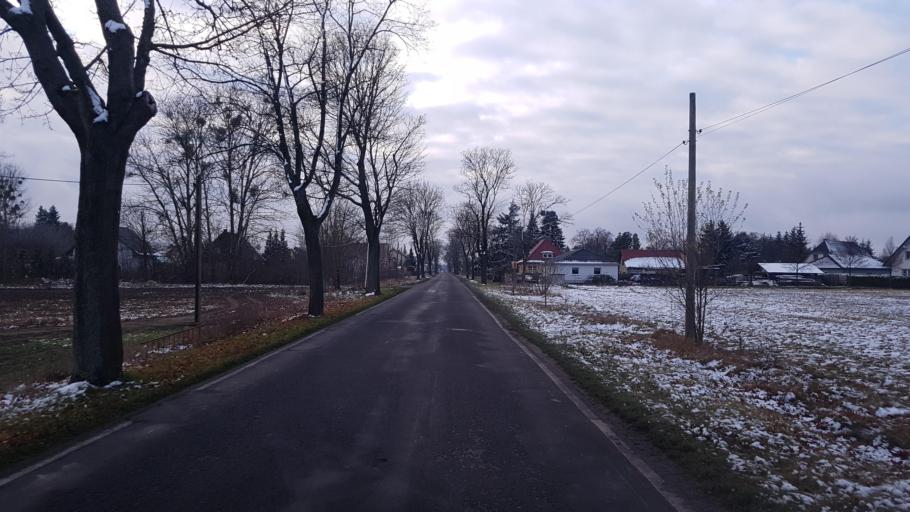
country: DE
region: Brandenburg
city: Rehfelde
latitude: 52.5095
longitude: 13.8679
